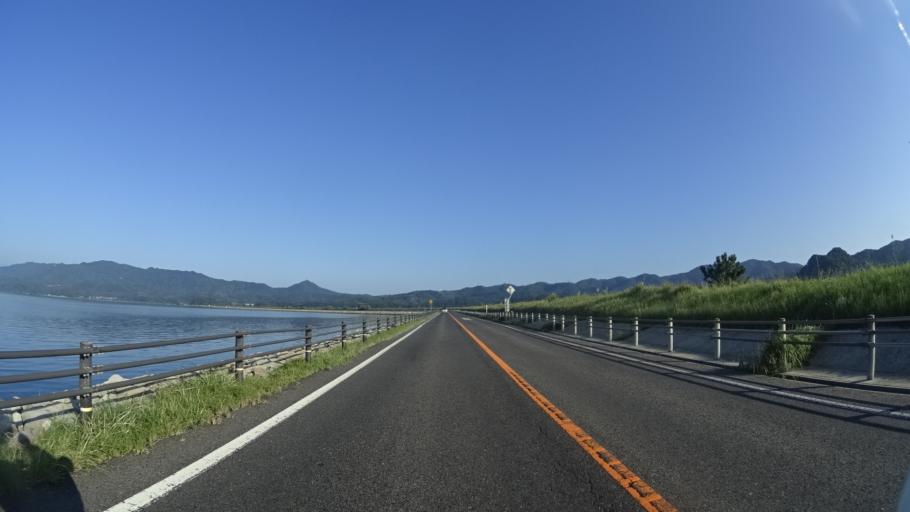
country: JP
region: Shimane
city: Sakaiminato
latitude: 35.5221
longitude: 133.1815
